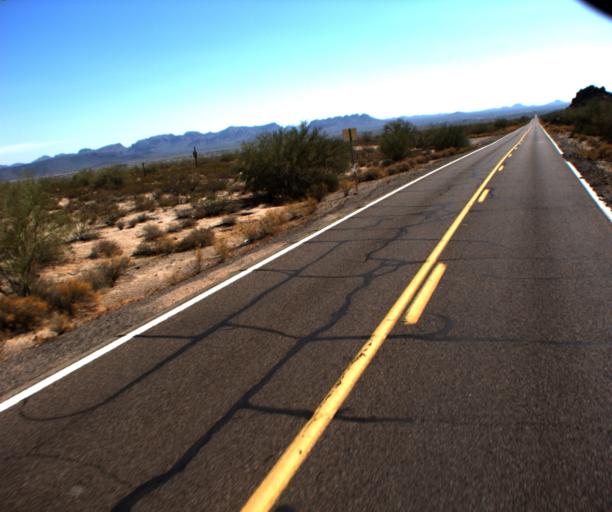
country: US
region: Arizona
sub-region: Pinal County
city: Sacaton
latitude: 33.0414
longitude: -111.7265
